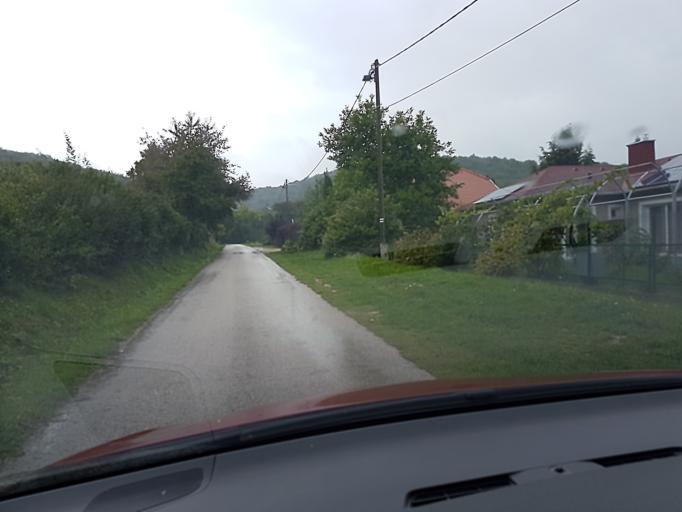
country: HU
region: Komarom-Esztergom
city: Pilismarot
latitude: 47.7804
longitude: 18.8671
